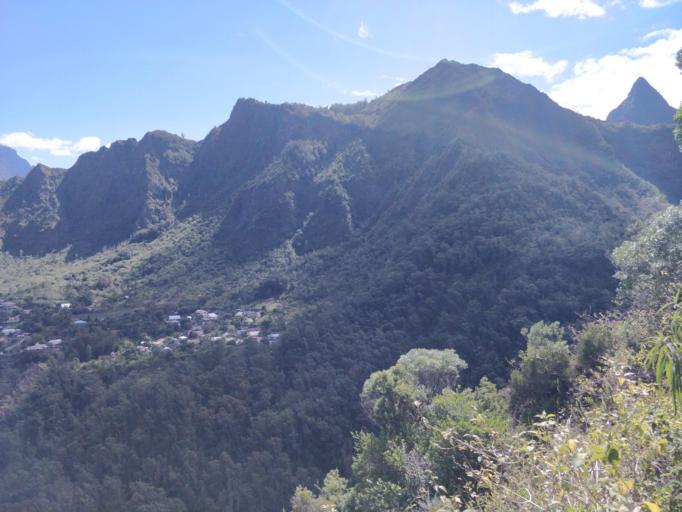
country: RE
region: Reunion
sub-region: Reunion
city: Cilaos
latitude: -21.1706
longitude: 55.4855
